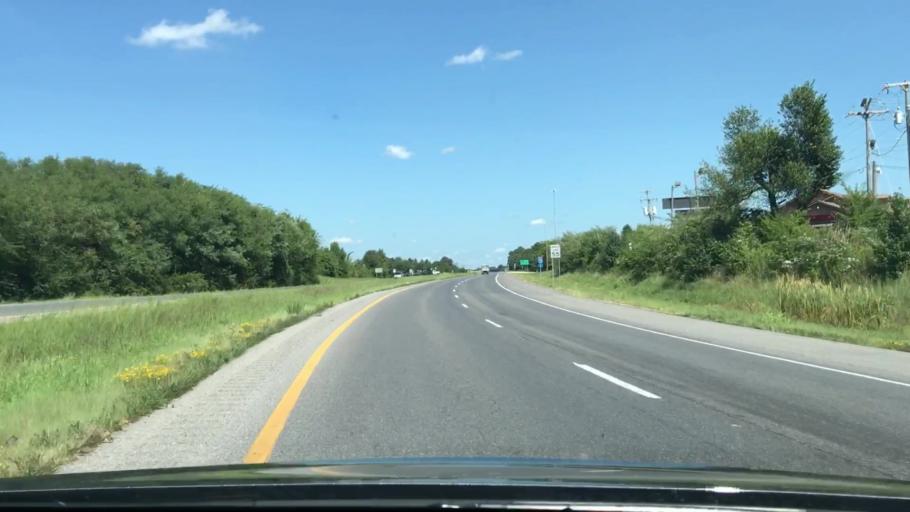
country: US
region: Kentucky
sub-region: McCracken County
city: Reidland
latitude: 36.9903
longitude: -88.5053
